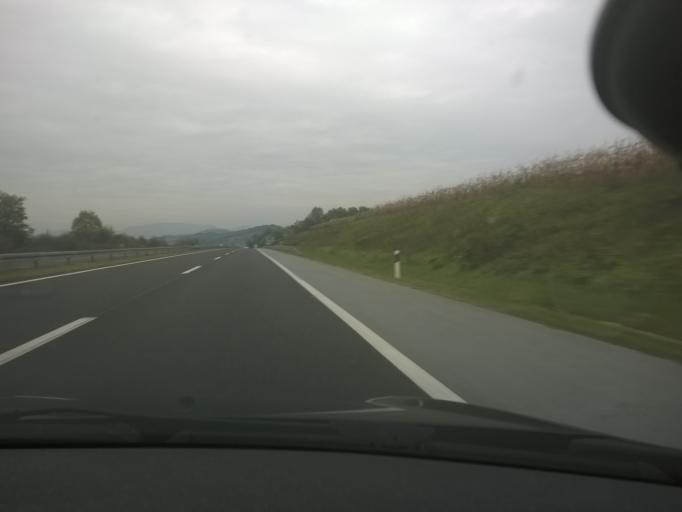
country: HR
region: Krapinsko-Zagorska
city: Zabok
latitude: 46.0593
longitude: 15.9193
